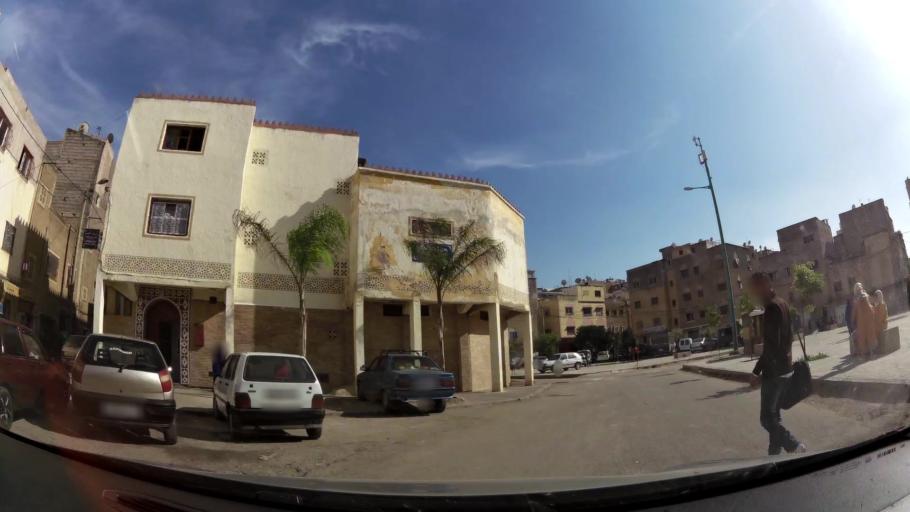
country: MA
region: Fes-Boulemane
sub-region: Fes
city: Fes
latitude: 34.0181
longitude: -5.0347
